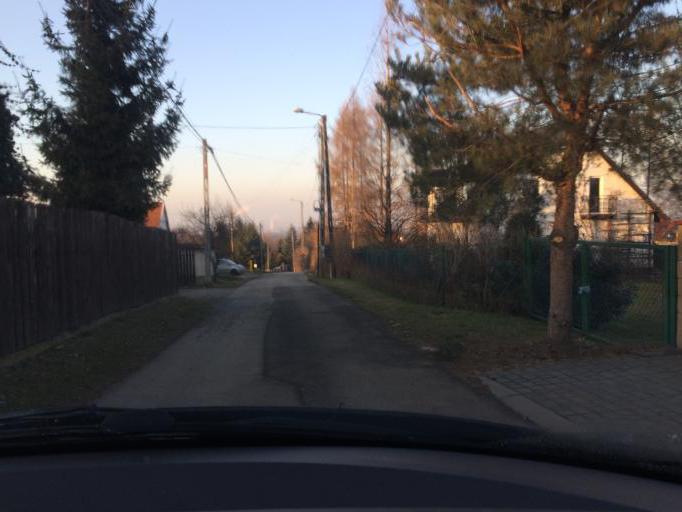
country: PL
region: Lesser Poland Voivodeship
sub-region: Powiat wielicki
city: Czarnochowice
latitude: 50.0022
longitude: 20.0402
